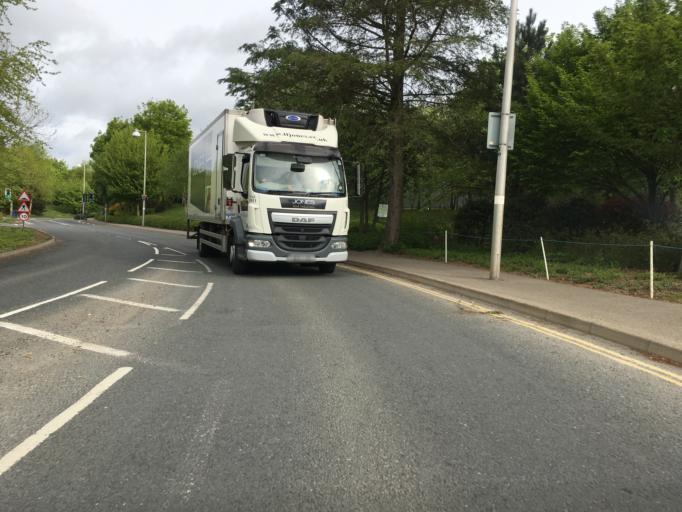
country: GB
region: England
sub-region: Bath and North East Somerset
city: Bath
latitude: 51.3765
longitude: -2.3244
